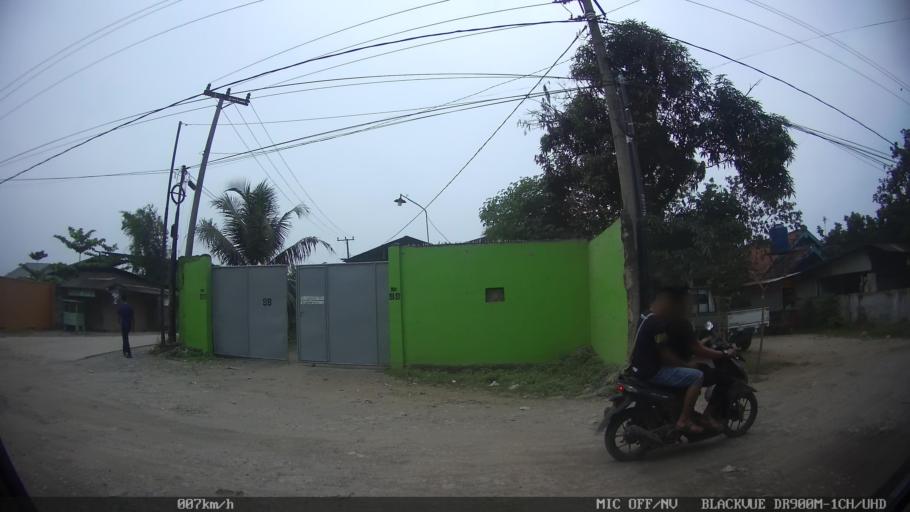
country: ID
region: Lampung
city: Panjang
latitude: -5.4374
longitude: 105.3233
